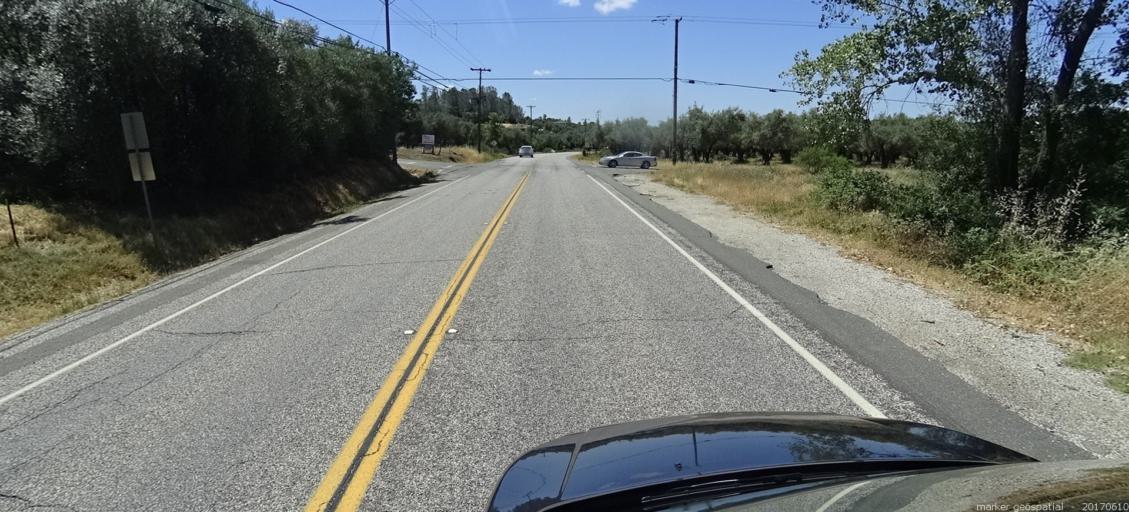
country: US
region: California
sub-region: Butte County
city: Oroville East
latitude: 39.4924
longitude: -121.4569
